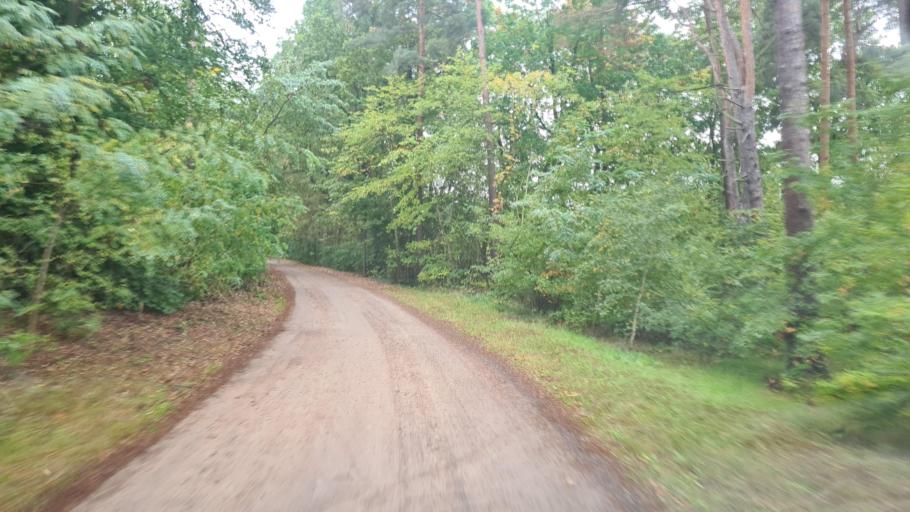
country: DE
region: Brandenburg
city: Storkow
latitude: 52.2286
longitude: 13.9335
